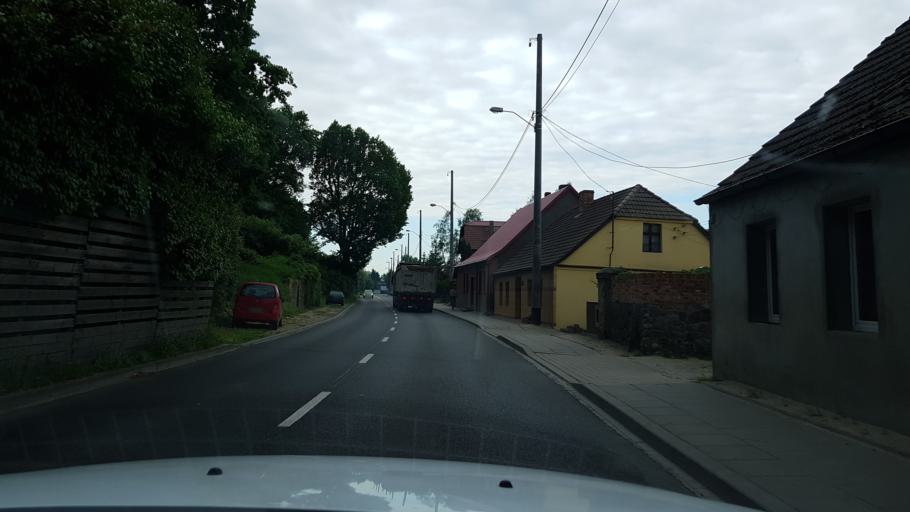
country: PL
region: West Pomeranian Voivodeship
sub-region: Powiat gryfinski
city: Gryfino
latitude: 53.3140
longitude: 14.5339
